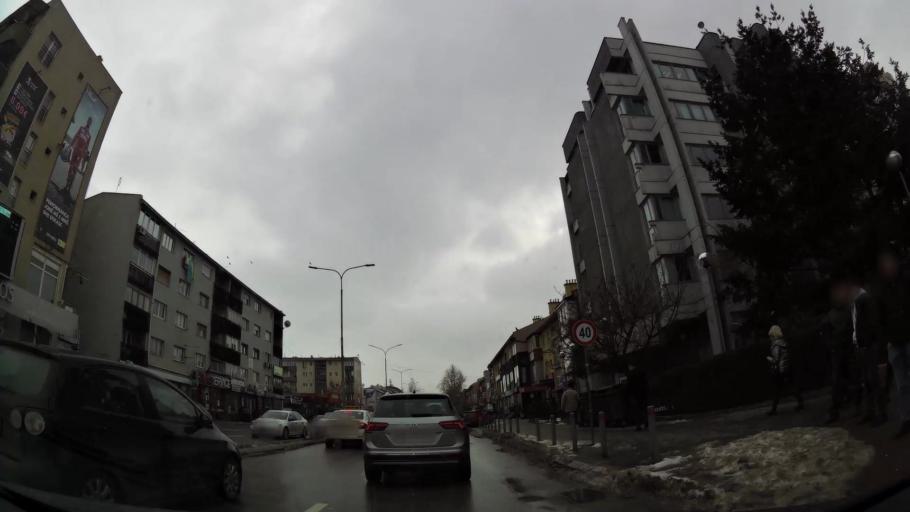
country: XK
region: Pristina
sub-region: Komuna e Prishtines
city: Pristina
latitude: 42.6555
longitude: 21.1596
